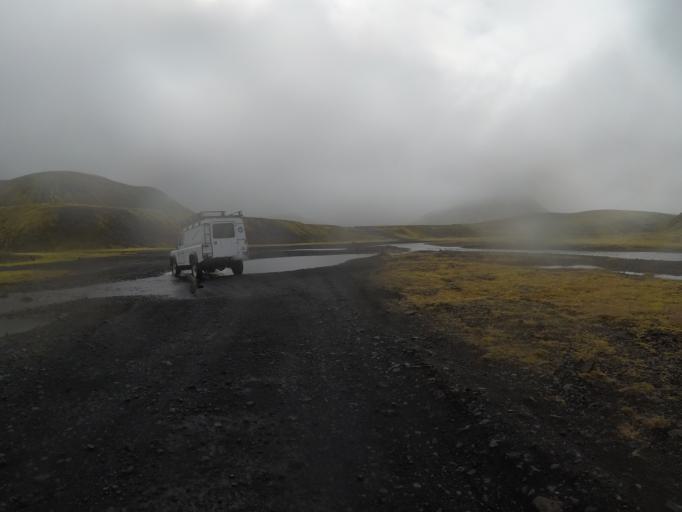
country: IS
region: South
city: Vestmannaeyjar
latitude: 63.9730
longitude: -18.7936
